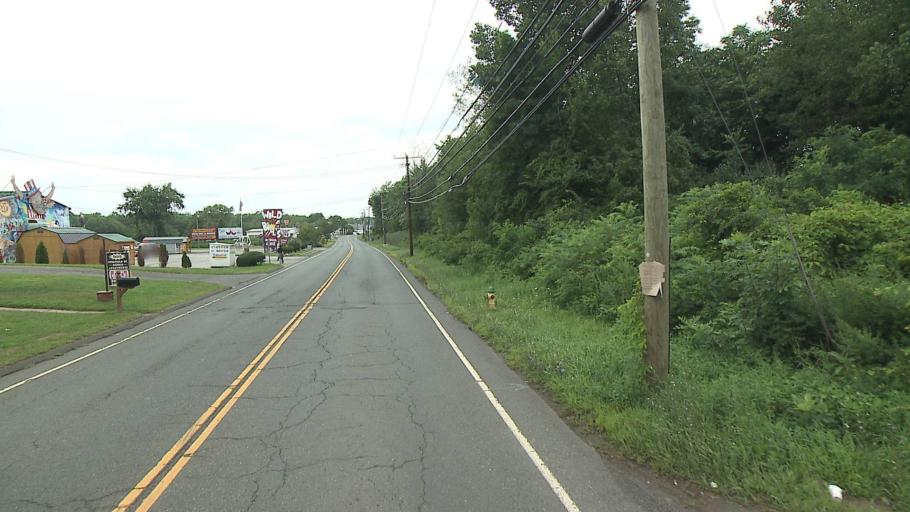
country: US
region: Connecticut
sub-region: Middlesex County
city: Cromwell
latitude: 41.5859
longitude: -72.6742
